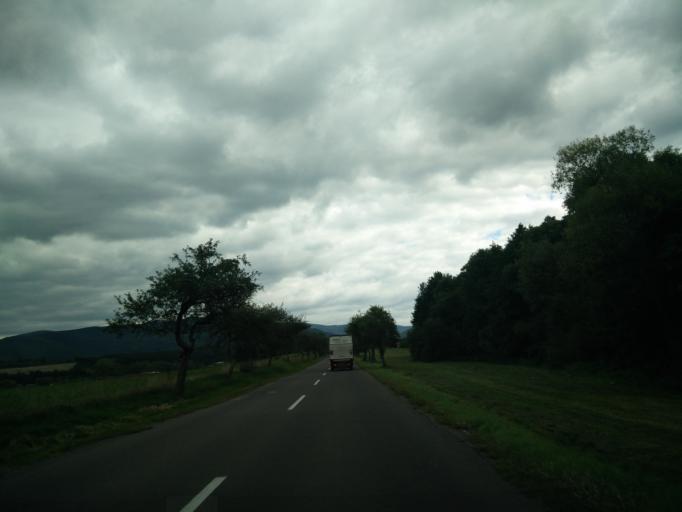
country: SK
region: Nitriansky
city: Partizanske
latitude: 48.6196
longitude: 18.4678
